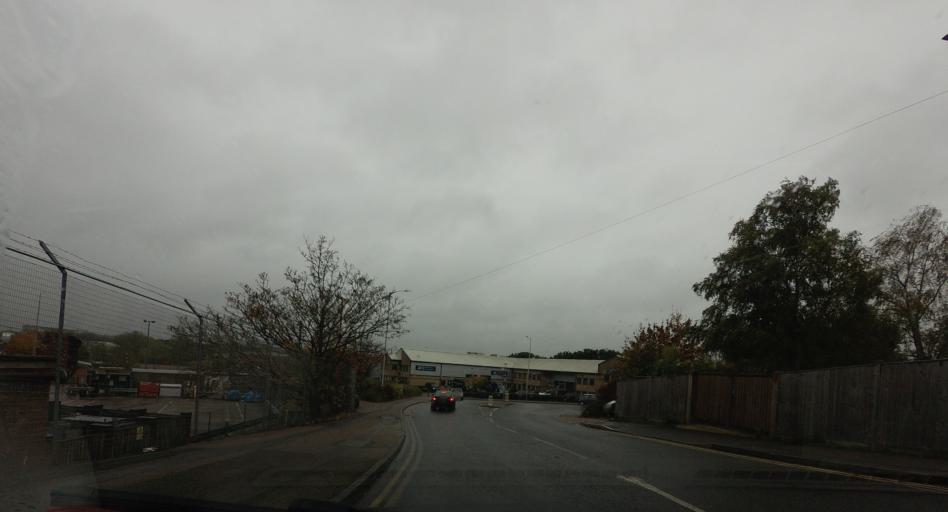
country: GB
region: England
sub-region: Kent
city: Tonbridge
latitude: 51.1902
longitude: 0.2882
